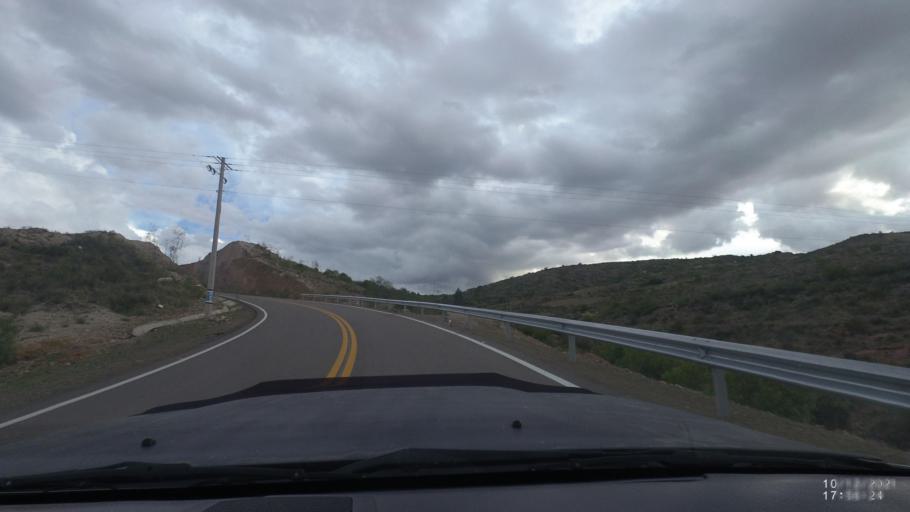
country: BO
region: Cochabamba
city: Cliza
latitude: -17.7263
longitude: -65.9311
